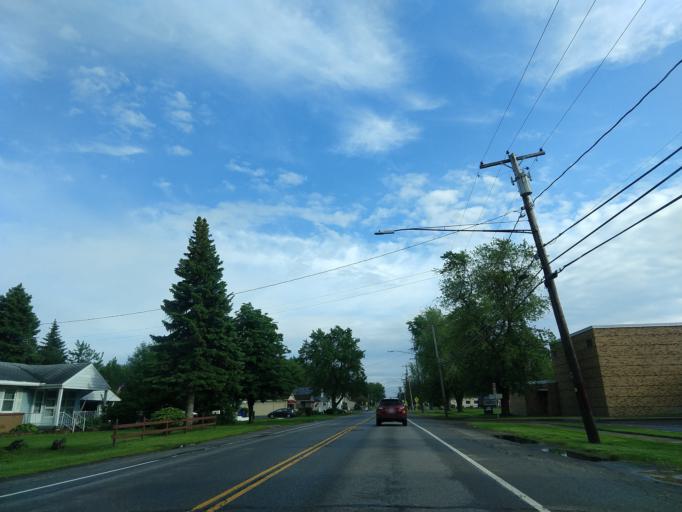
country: US
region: New York
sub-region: Erie County
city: West Seneca
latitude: 42.8612
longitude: -78.7875
